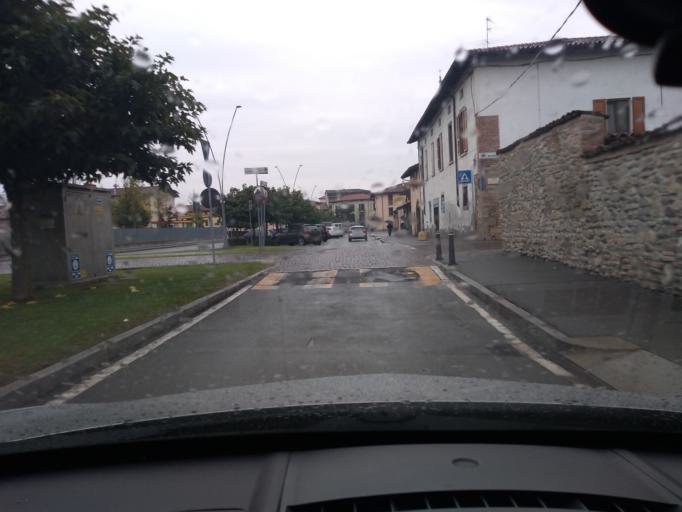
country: IT
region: Lombardy
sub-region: Provincia di Bergamo
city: Mornico al Serio
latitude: 45.5939
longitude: 9.8090
